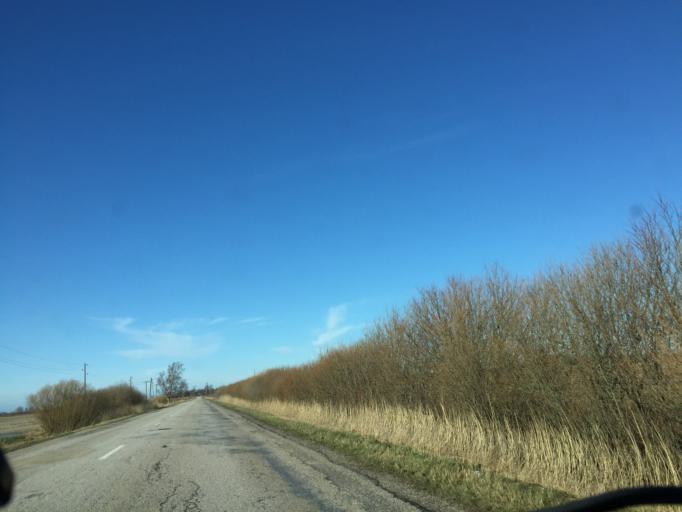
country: LV
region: Ventspils Rajons
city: Piltene
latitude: 57.3020
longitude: 21.6440
